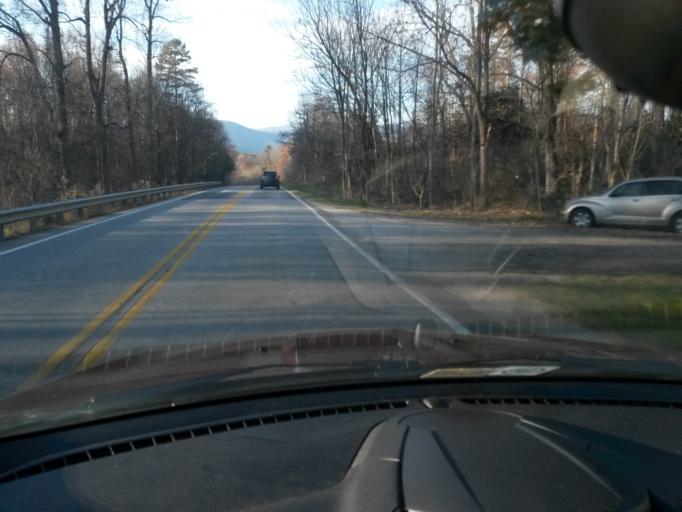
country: US
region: Virginia
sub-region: Amherst County
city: Amherst
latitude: 37.6552
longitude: -79.1389
